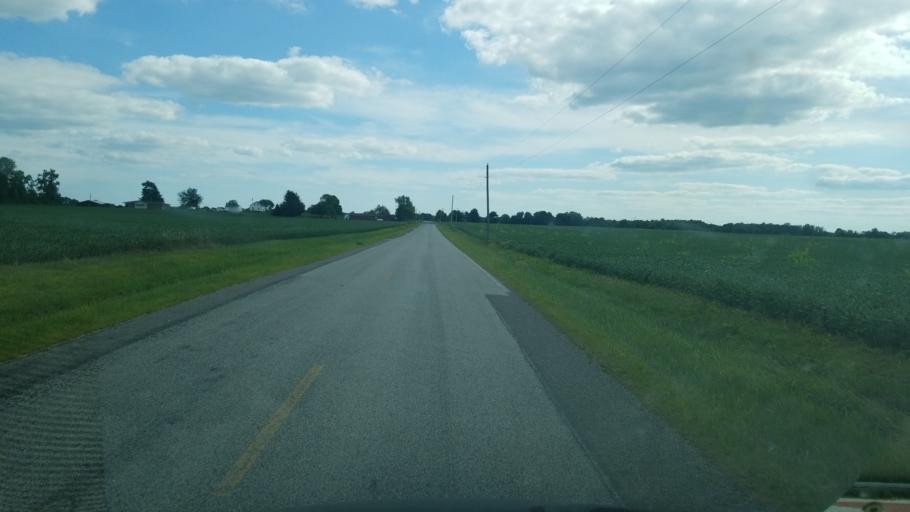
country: US
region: Ohio
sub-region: Champaign County
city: Saint Paris
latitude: 40.2003
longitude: -83.9430
